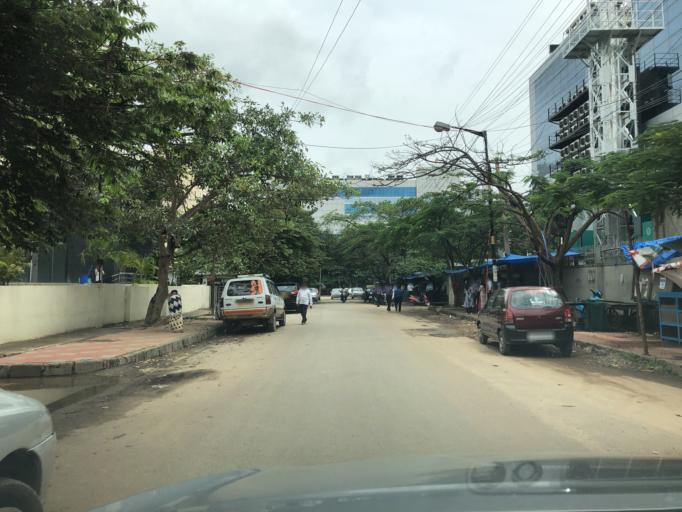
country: IN
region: Karnataka
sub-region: Bangalore Rural
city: Hoskote
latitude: 12.9792
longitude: 77.7248
